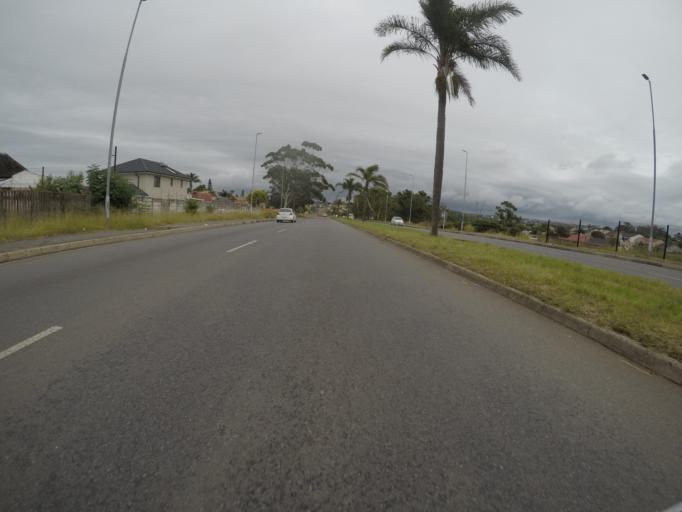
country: ZA
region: Eastern Cape
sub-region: Buffalo City Metropolitan Municipality
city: East London
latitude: -32.9968
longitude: 27.8886
